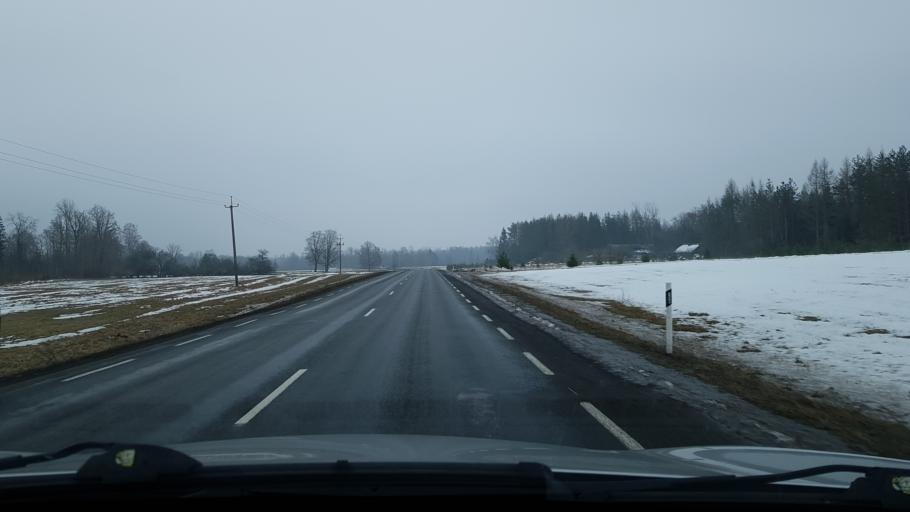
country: EE
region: Viljandimaa
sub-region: Viiratsi vald
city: Viiratsi
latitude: 58.2489
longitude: 25.7718
